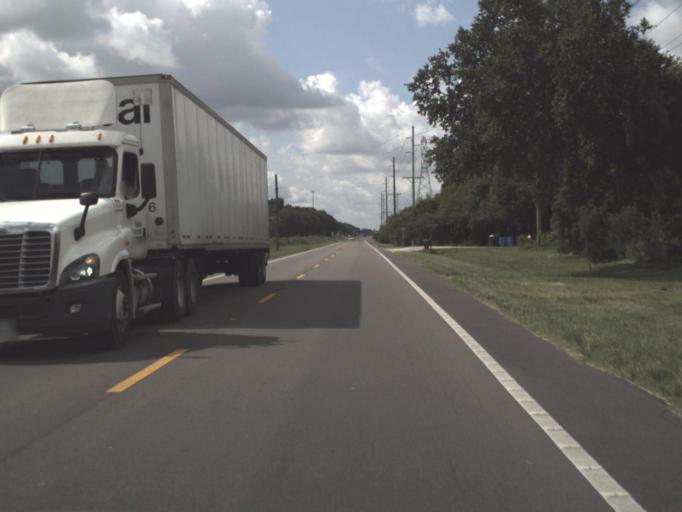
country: US
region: Florida
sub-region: Hillsborough County
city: Plant City
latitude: 28.0845
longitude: -82.1395
